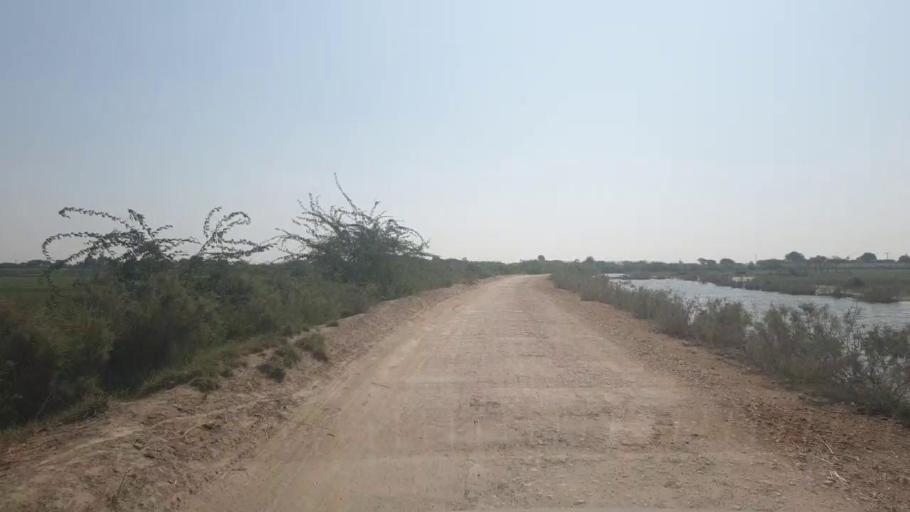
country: PK
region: Sindh
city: Badin
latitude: 24.6500
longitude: 68.9169
